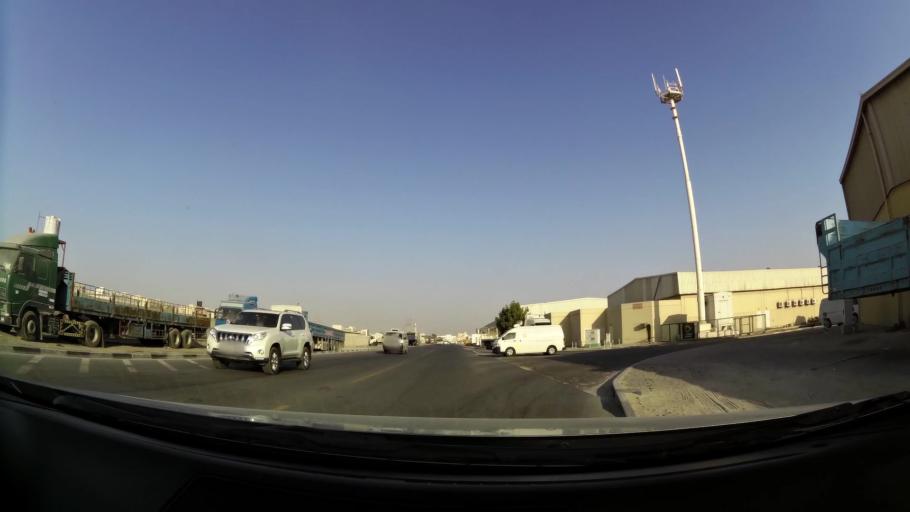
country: AE
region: Dubai
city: Dubai
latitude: 25.1372
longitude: 55.2459
